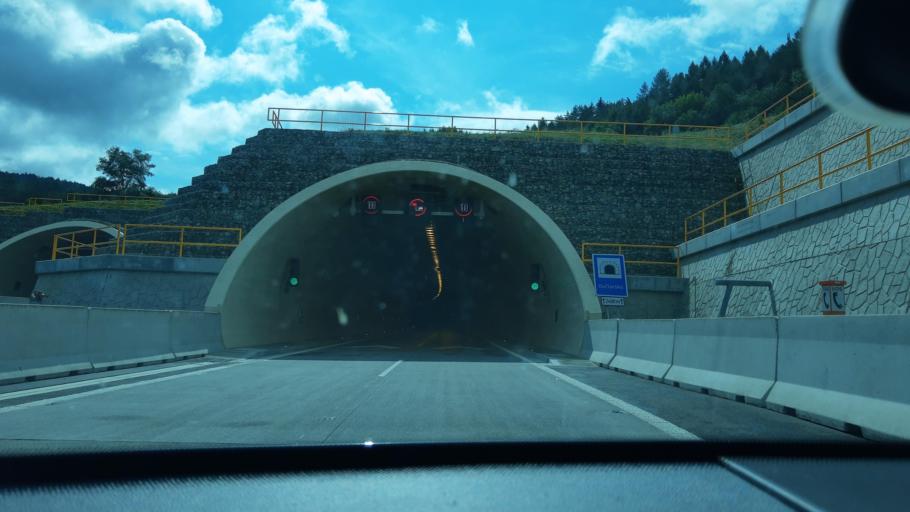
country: SK
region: Zilinsky
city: Bytca
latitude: 49.2231
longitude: 18.6353
